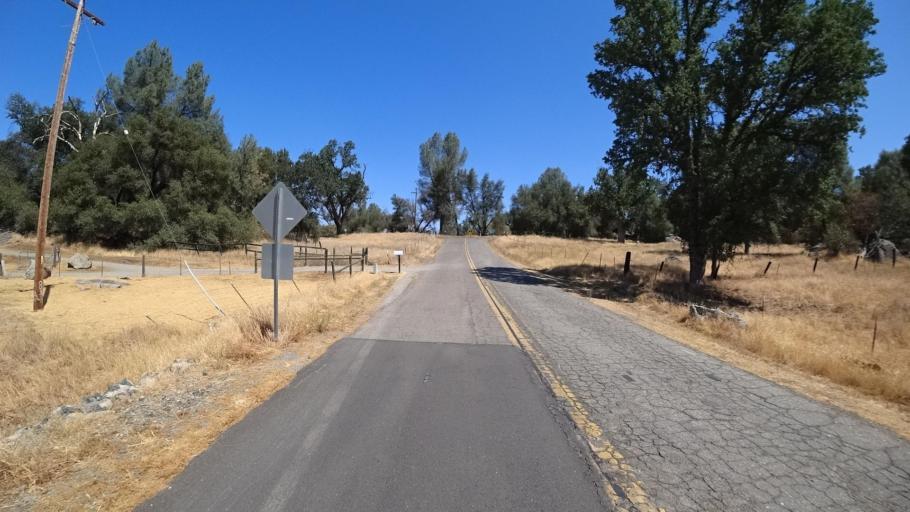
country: US
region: California
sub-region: Mariposa County
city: Mariposa
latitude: 37.4209
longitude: -119.9663
